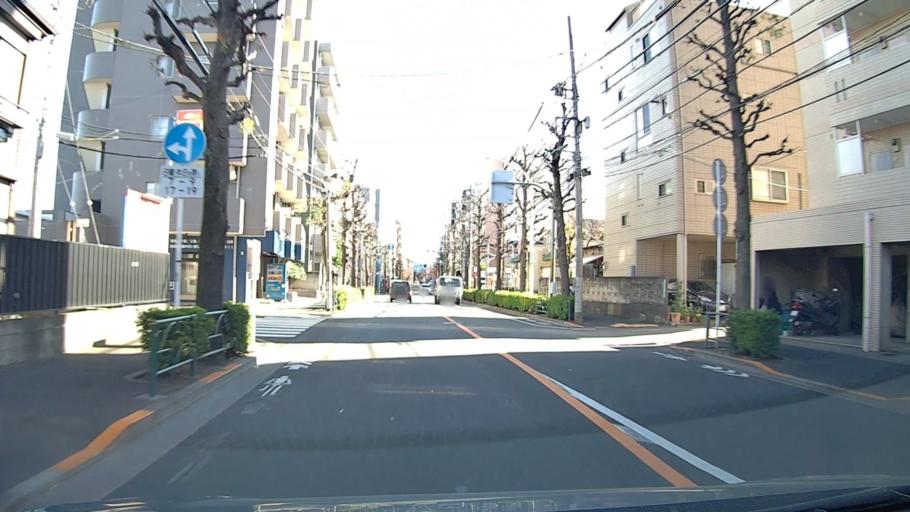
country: JP
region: Tokyo
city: Tokyo
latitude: 35.7240
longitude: 139.6480
